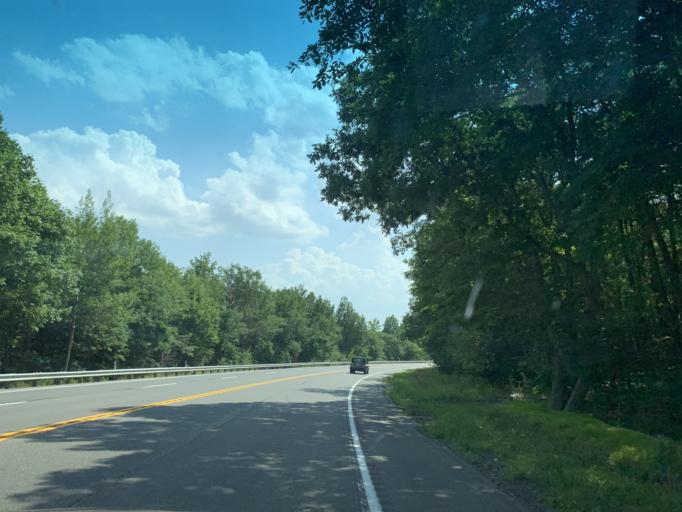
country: US
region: Pennsylvania
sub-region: Schuylkill County
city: Ashland
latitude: 40.8110
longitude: -76.3335
